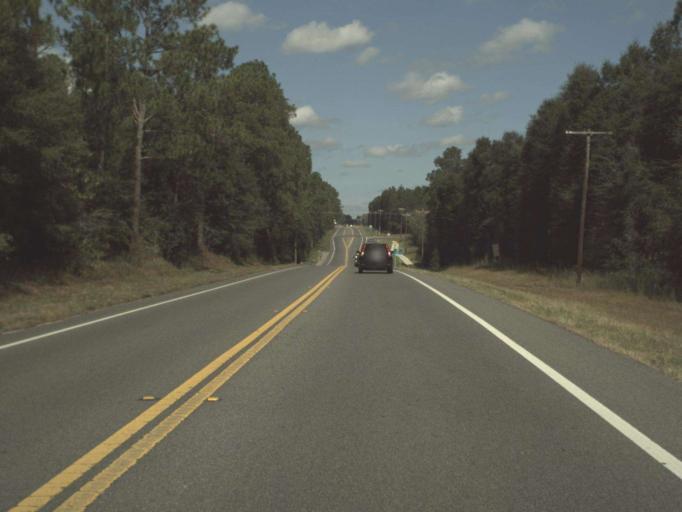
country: US
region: Florida
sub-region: Walton County
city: DeFuniak Springs
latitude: 30.7718
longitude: -86.1130
